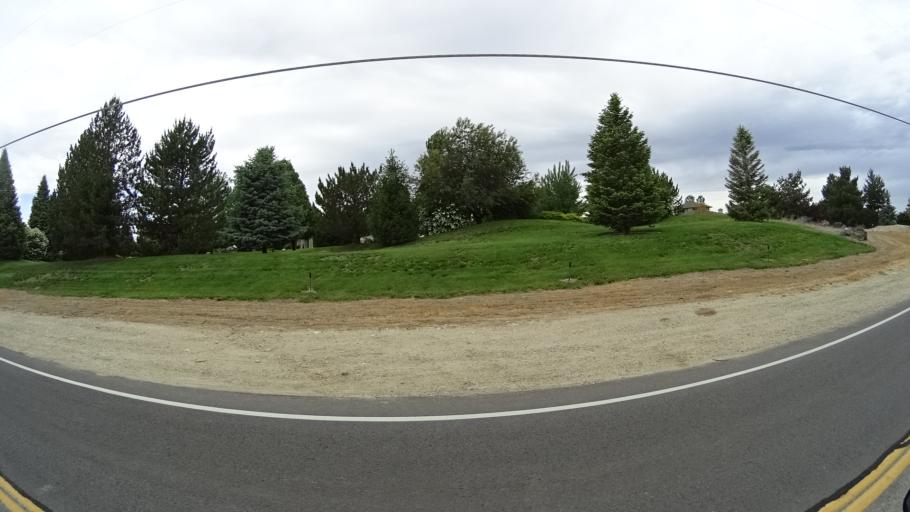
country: US
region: Idaho
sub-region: Ada County
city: Meridian
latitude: 43.5806
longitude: -116.4137
